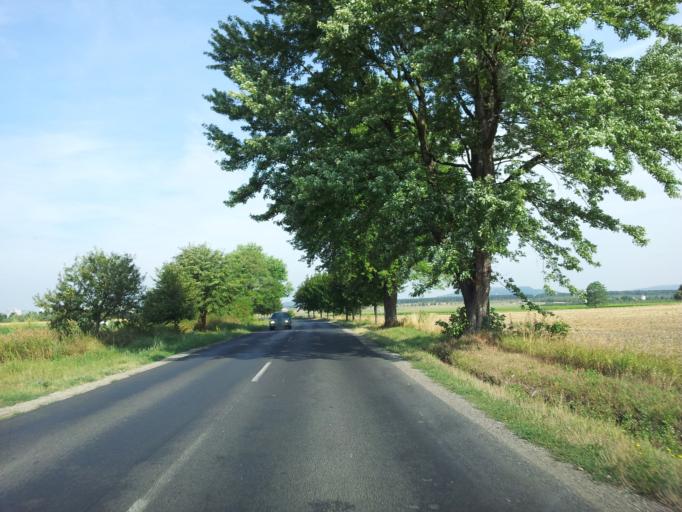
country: HU
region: Veszprem
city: Tapolca
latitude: 46.8723
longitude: 17.4709
